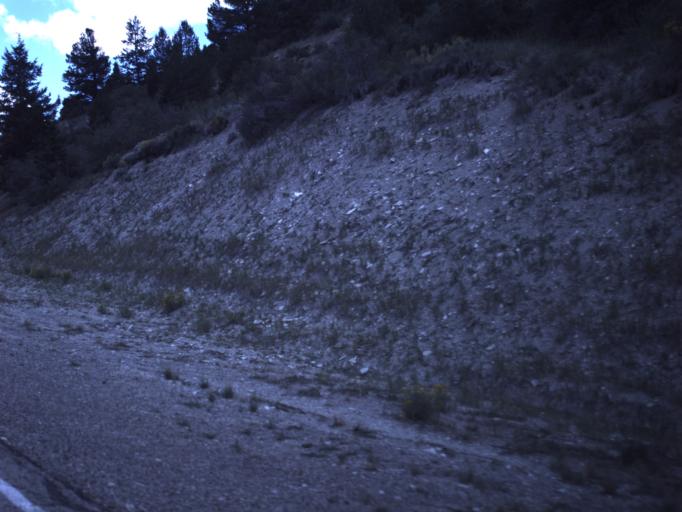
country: US
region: Utah
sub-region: Carbon County
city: Helper
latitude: 39.9026
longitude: -110.7254
